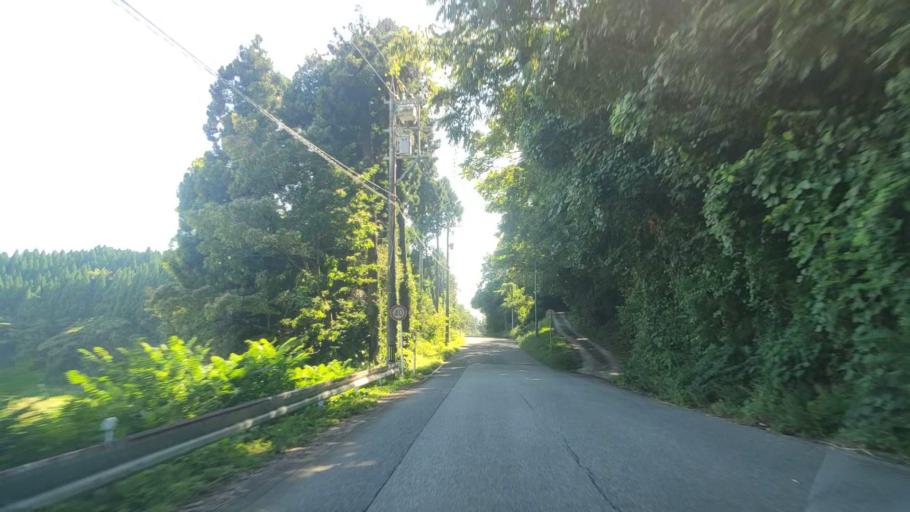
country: JP
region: Ishikawa
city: Nanao
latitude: 37.4771
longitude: 137.3349
